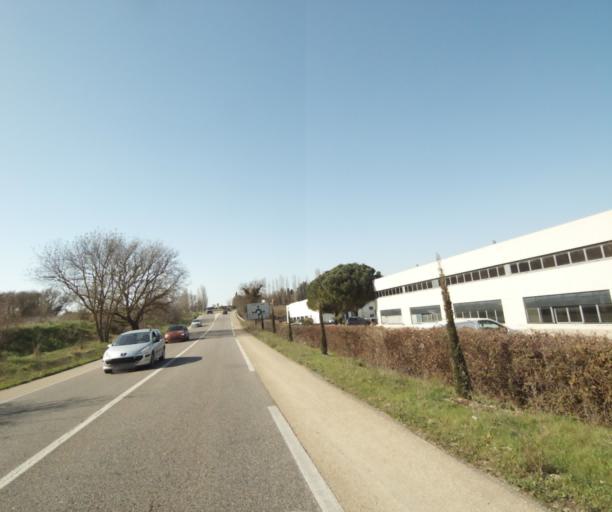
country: FR
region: Provence-Alpes-Cote d'Azur
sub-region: Departement des Bouches-du-Rhone
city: Cabries
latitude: 43.4259
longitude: 5.3950
